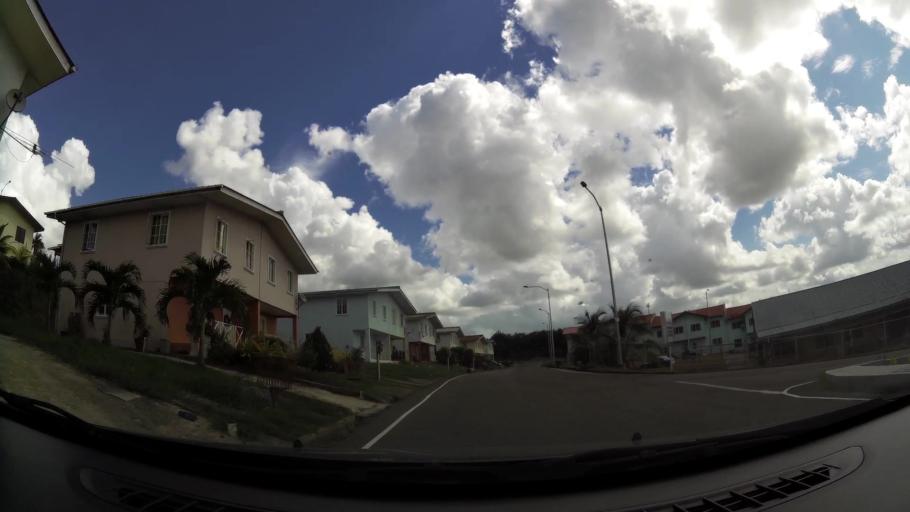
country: TT
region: City of San Fernando
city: Mon Repos
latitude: 10.2558
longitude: -61.4422
